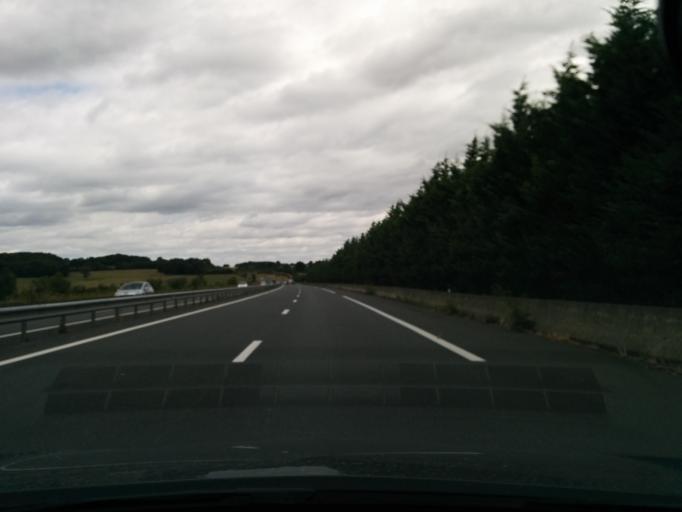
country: FR
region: Centre
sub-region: Departement de l'Indre
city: Le Pechereau
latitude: 46.5214
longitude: 1.5145
